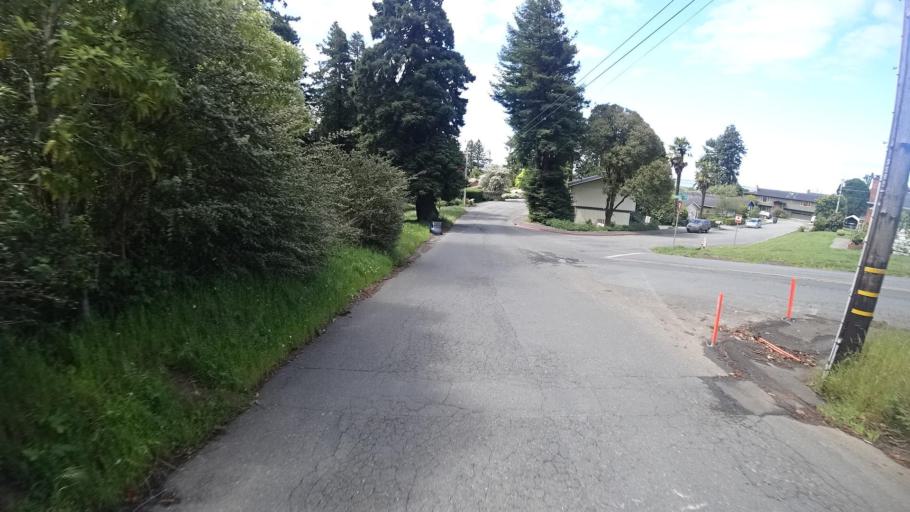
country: US
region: California
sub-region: Humboldt County
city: Arcata
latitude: 40.8666
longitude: -124.0757
